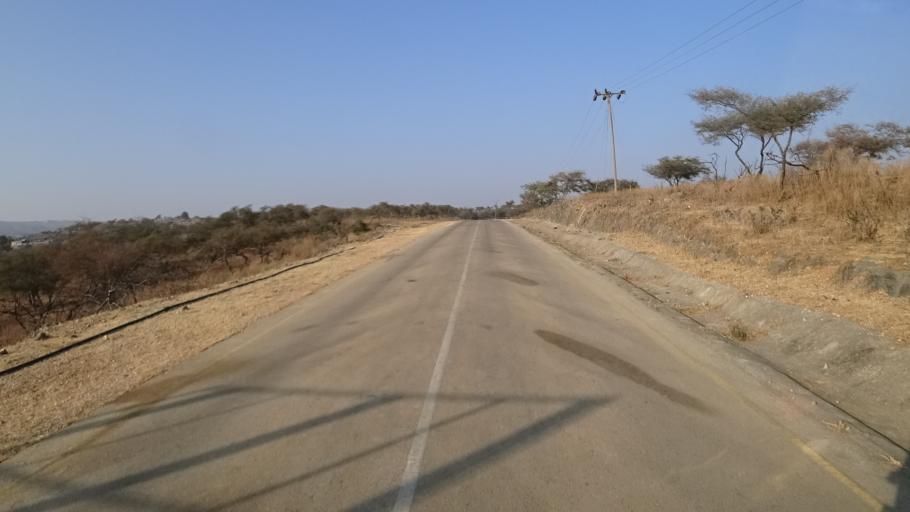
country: YE
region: Al Mahrah
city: Hawf
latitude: 16.7724
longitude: 53.3356
